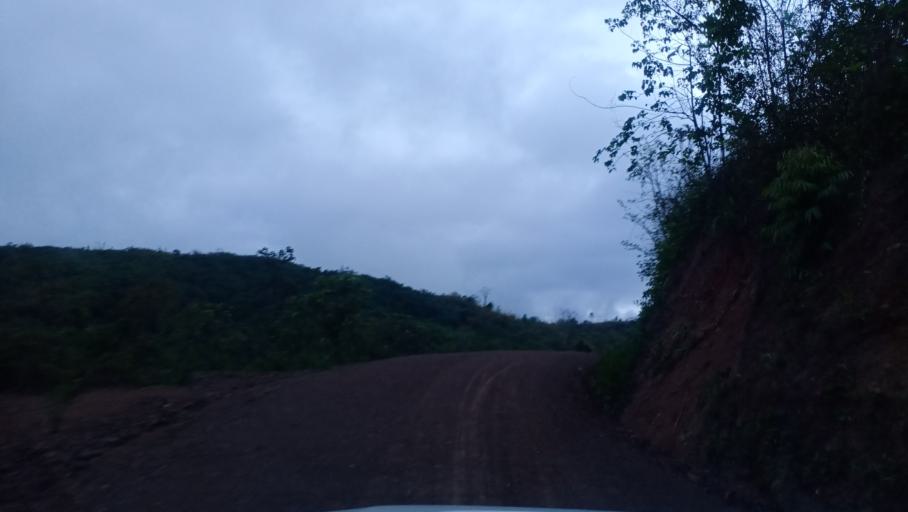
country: VN
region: Huyen Dien Bien
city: Dien Bien Phu
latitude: 21.3480
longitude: 102.7206
